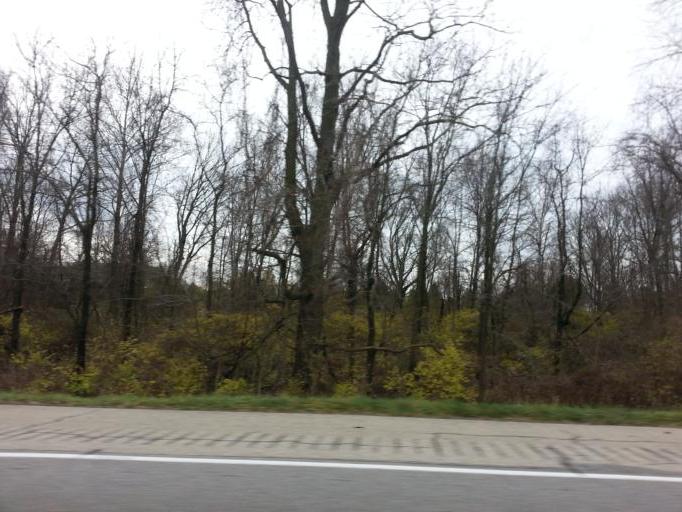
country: US
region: Indiana
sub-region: Decatur County
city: Greensburg
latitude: 39.3461
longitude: -85.4359
